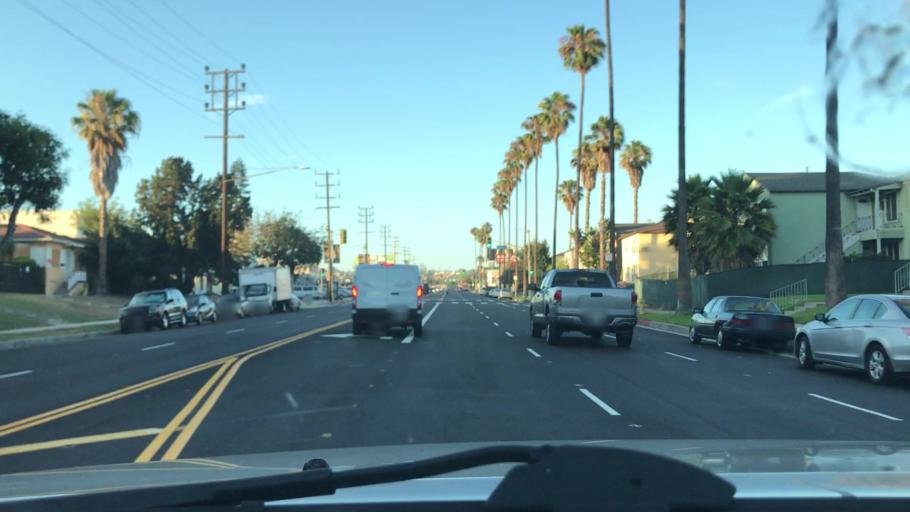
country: US
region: California
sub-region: Los Angeles County
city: Ladera Heights
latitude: 33.9745
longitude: -118.3750
